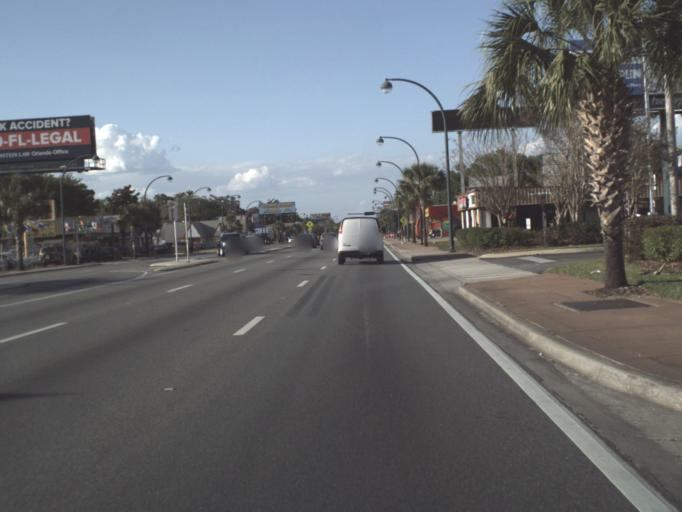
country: US
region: Florida
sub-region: Orange County
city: Holden Heights
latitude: 28.4977
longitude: -81.3968
